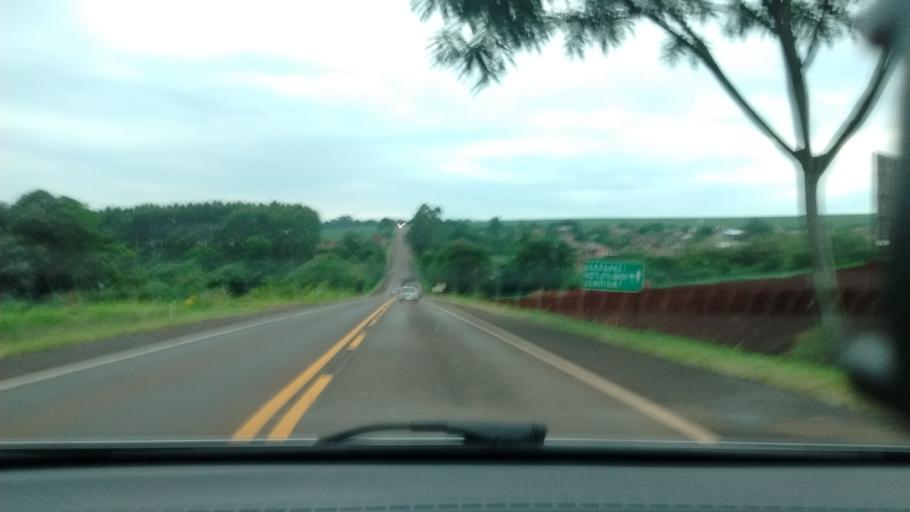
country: BR
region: Parana
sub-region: Corbelia
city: Corbelia
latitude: -24.8069
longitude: -53.2927
